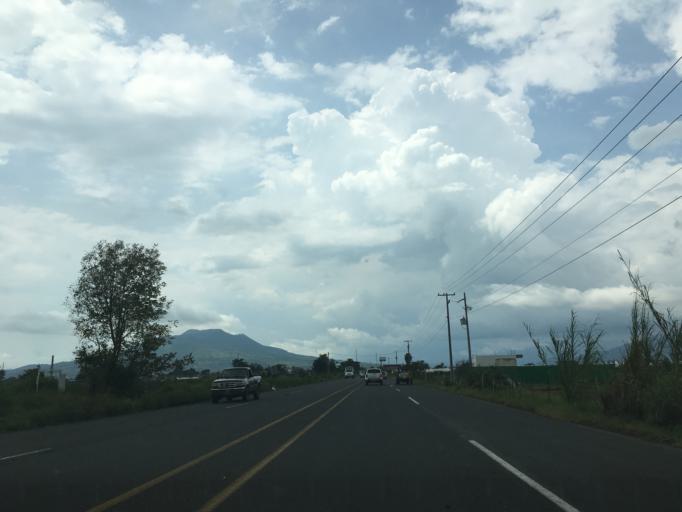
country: MX
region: Michoacan
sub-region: Periban
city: Gildardo Magana (Los Angeles)
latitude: 19.5757
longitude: -102.4713
